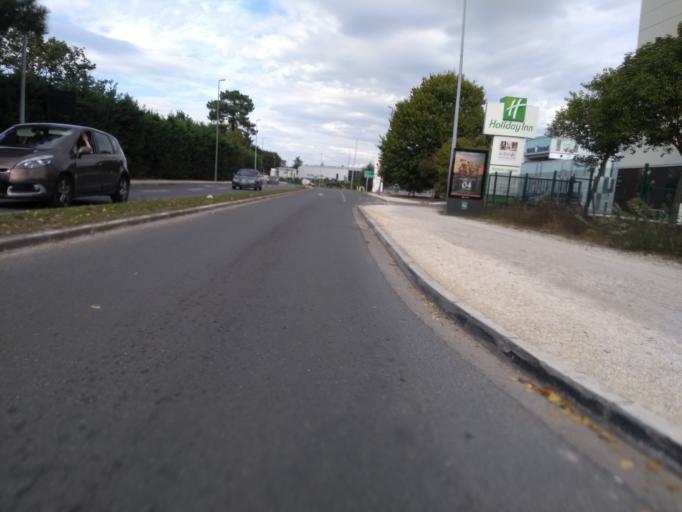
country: FR
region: Aquitaine
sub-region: Departement de la Gironde
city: Pessac
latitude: 44.7884
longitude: -0.6467
